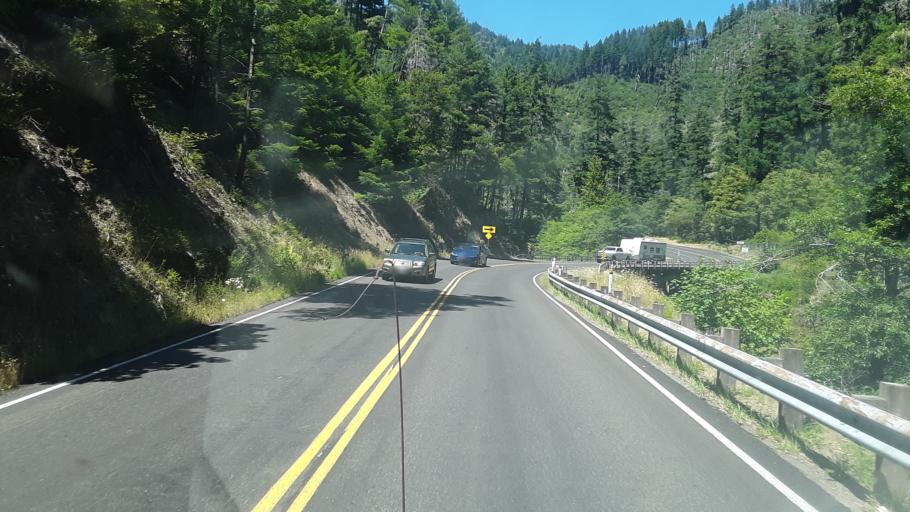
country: US
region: Oregon
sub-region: Josephine County
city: Cave Junction
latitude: 41.8790
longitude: -123.8272
